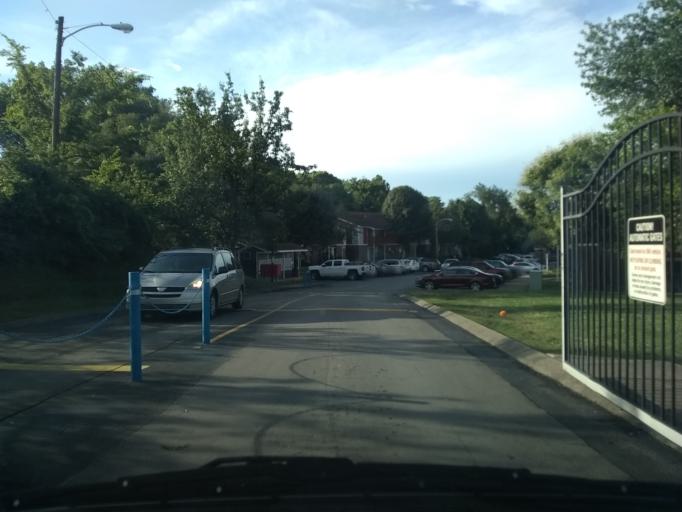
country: US
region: Tennessee
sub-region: Davidson County
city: Nashville
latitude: 36.1311
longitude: -86.7139
